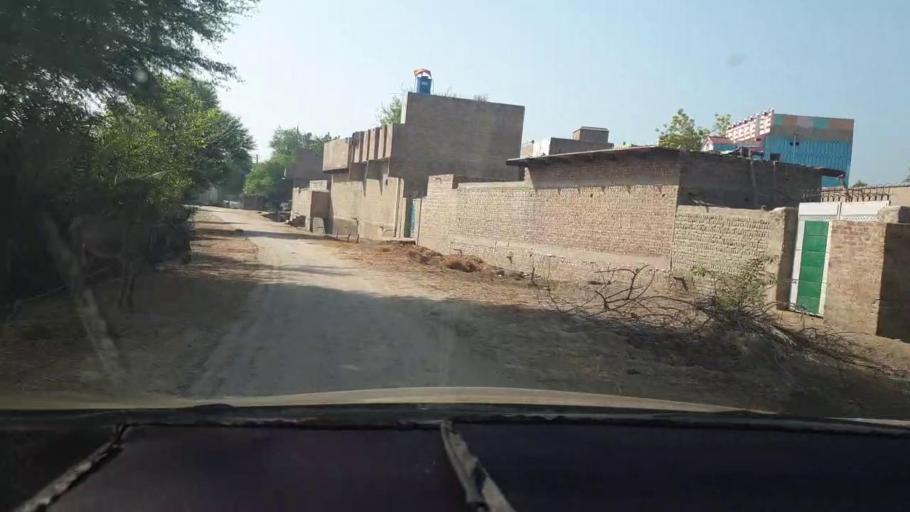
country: PK
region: Sindh
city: Kambar
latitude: 27.6087
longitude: 68.0923
